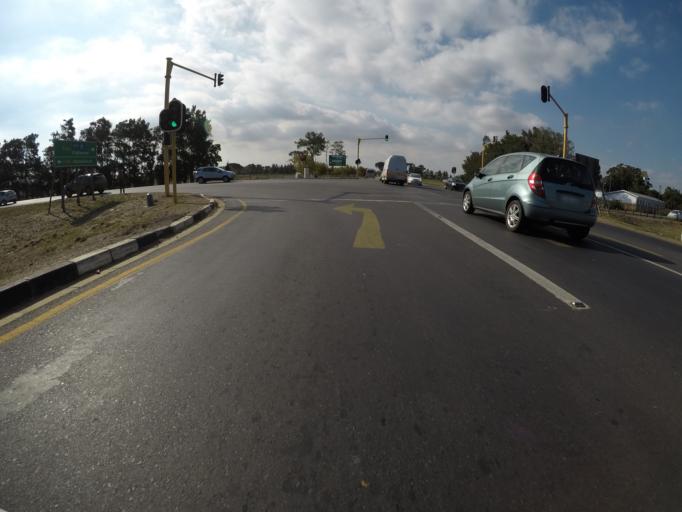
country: ZA
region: Western Cape
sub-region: Cape Winelands District Municipality
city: Stellenbosch
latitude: -33.8752
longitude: 18.8139
